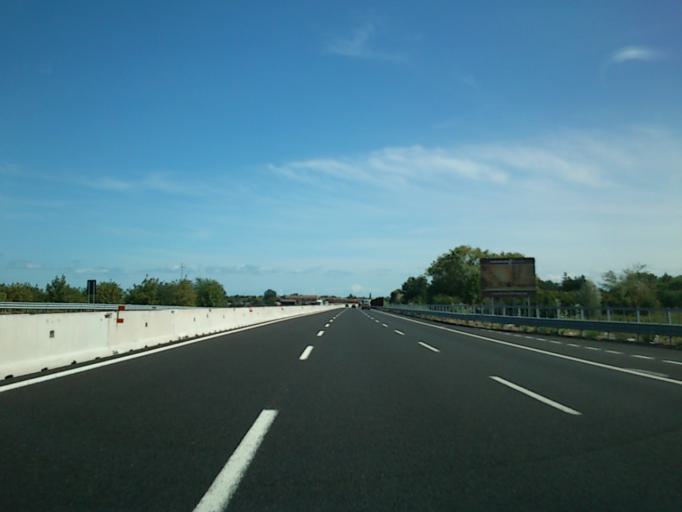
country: IT
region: The Marches
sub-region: Provincia di Pesaro e Urbino
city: Centinarola
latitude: 43.8392
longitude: 12.9840
